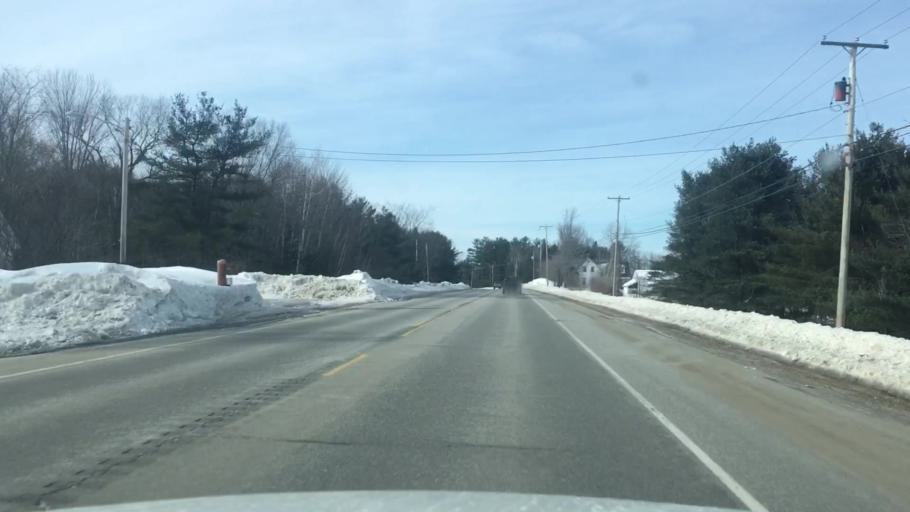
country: US
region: Maine
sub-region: Penobscot County
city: Kenduskeag
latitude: 44.9568
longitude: -68.9525
